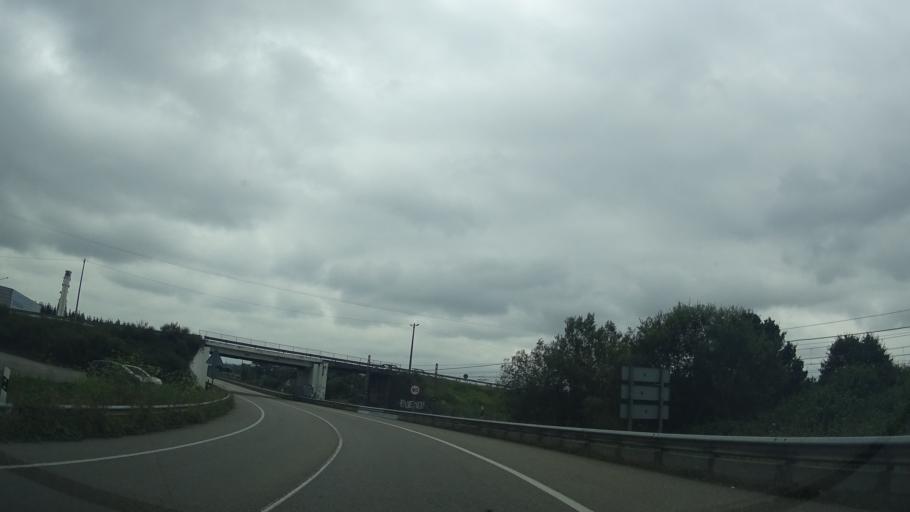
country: ES
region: Asturias
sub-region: Province of Asturias
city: Norena
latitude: 43.3816
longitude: -5.7441
